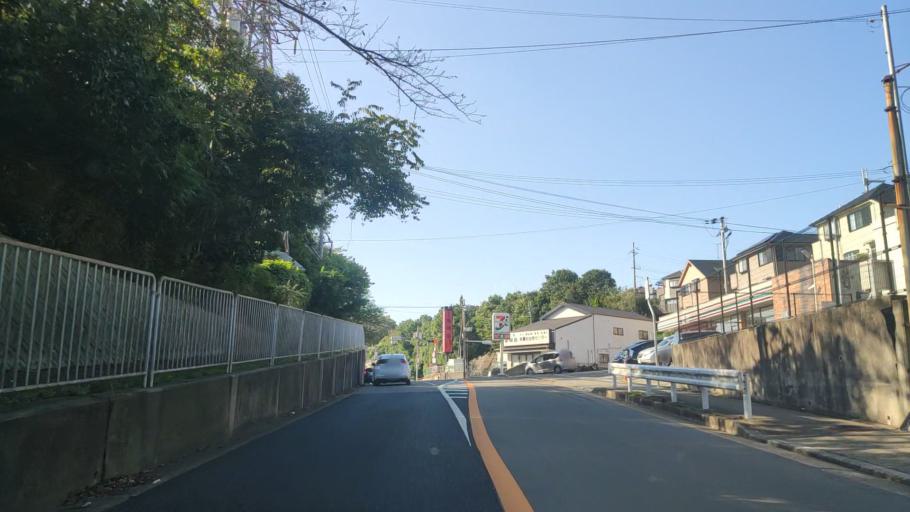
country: JP
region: Hyogo
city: Kobe
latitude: 34.7382
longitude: 135.1586
